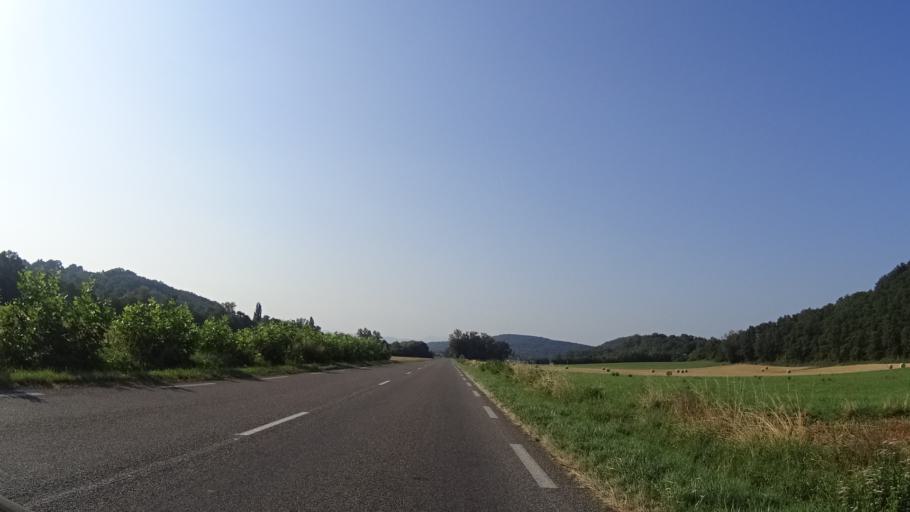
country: FR
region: Midi-Pyrenees
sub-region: Departement de l'Ariege
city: Mirepoix
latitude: 43.0639
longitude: 1.8808
